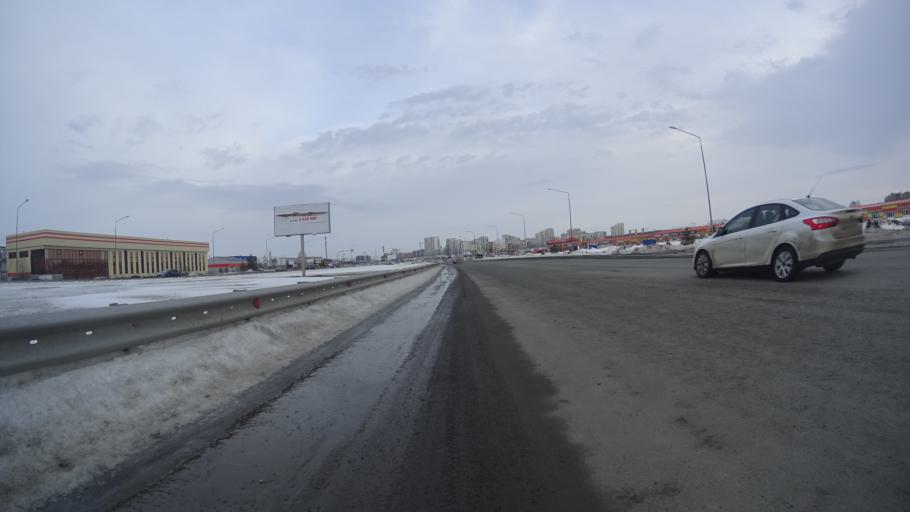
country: RU
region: Chelyabinsk
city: Roshchino
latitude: 55.1836
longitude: 61.2452
